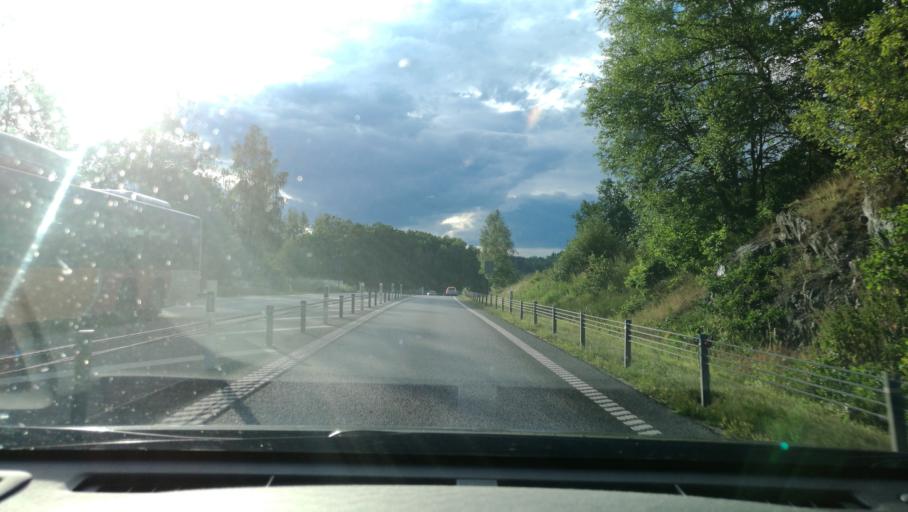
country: SE
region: OEstergoetland
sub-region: Norrkopings Kommun
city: Svartinge
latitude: 58.6863
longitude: 15.9331
